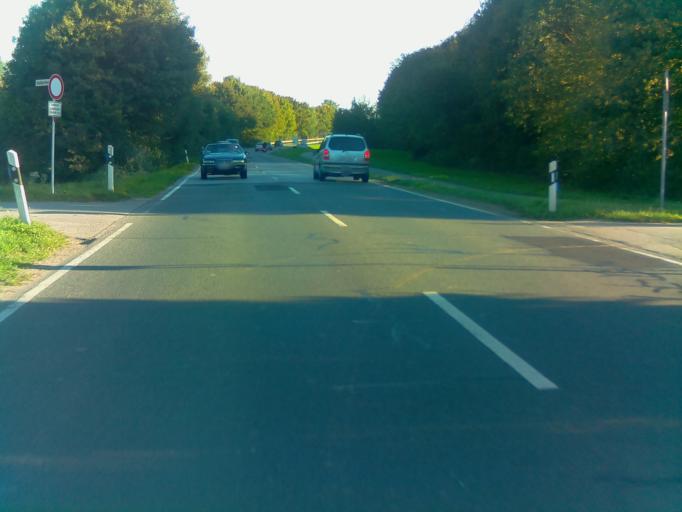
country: DE
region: Hesse
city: Zwingenberg
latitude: 49.7101
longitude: 8.6076
